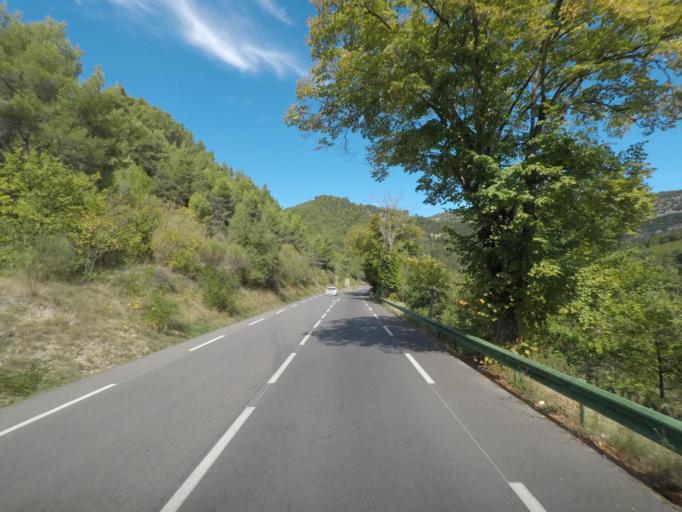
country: FR
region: Rhone-Alpes
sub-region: Departement de la Drome
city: Nyons
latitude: 44.3795
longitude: 5.1710
